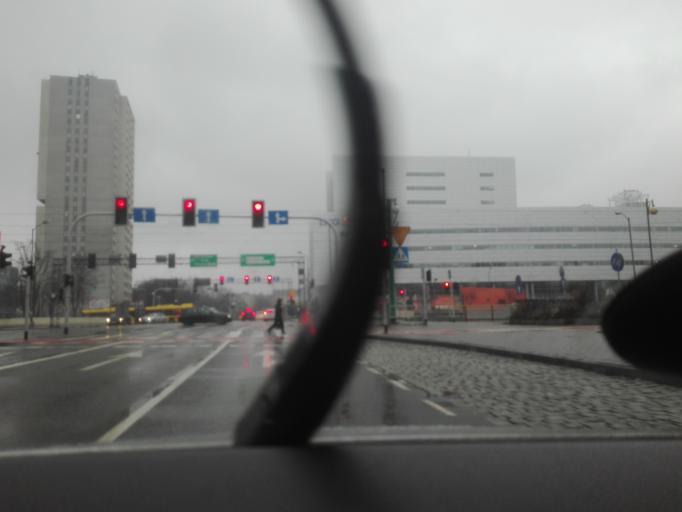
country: PL
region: Silesian Voivodeship
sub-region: Katowice
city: Katowice
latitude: 50.2660
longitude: 19.0192
